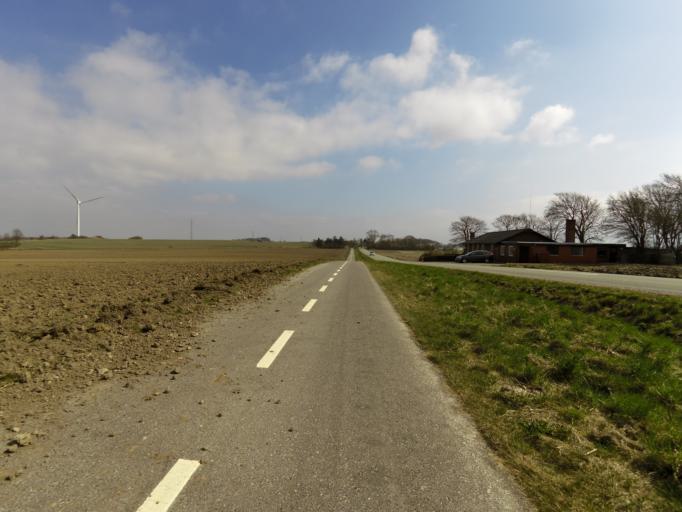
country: DK
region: Central Jutland
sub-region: Struer Kommune
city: Struer
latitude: 56.4556
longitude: 8.6112
